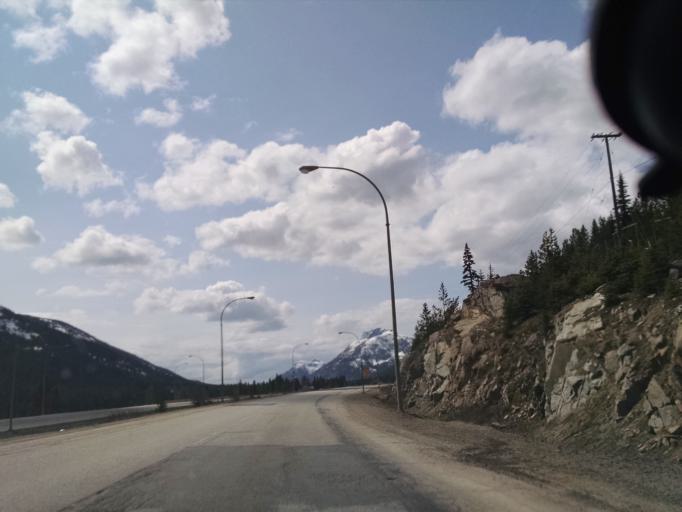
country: CA
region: British Columbia
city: Hope
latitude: 49.6341
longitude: -121.0100
